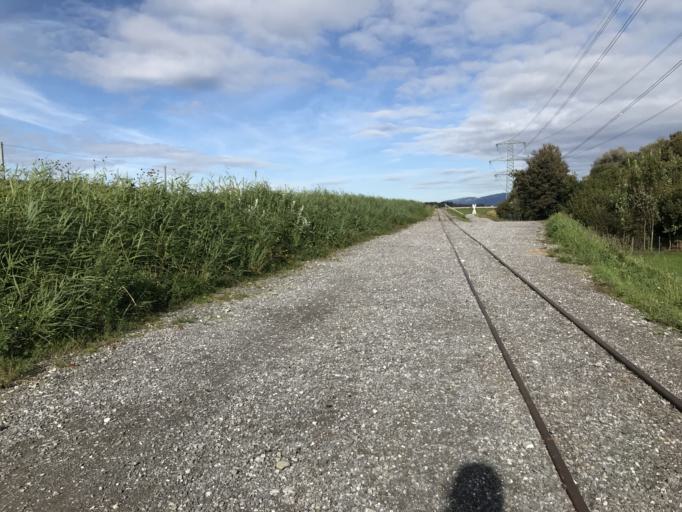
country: AT
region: Vorarlberg
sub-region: Politischer Bezirk Feldkirch
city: Mader
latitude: 47.3480
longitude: 9.6041
